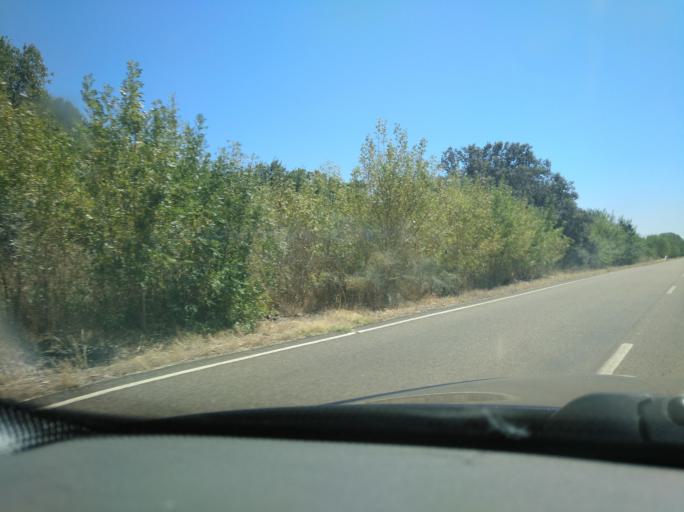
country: ES
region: Extremadura
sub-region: Provincia de Badajoz
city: Olivenza
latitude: 38.7180
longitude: -7.2003
